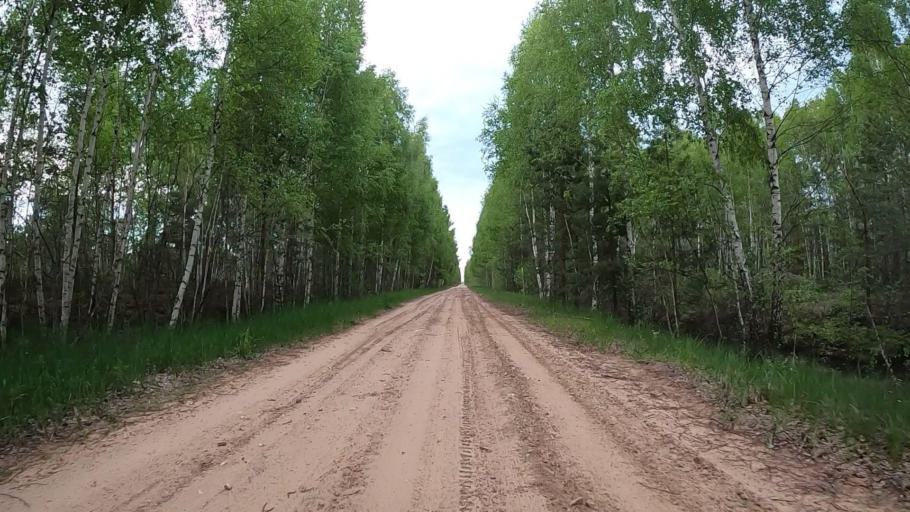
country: LV
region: Olaine
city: Olaine
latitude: 56.8472
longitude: 23.9389
